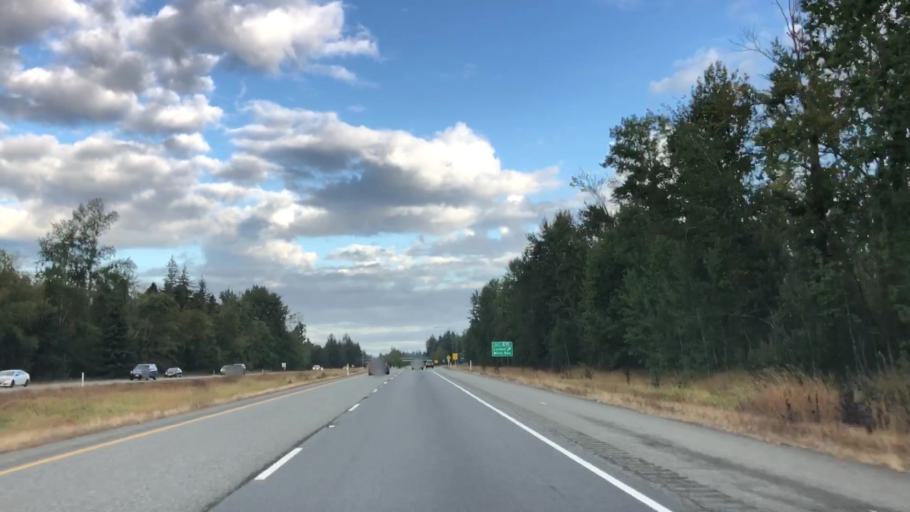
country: US
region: Washington
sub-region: Whatcom County
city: Birch Bay
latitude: 48.9321
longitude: -122.6546
